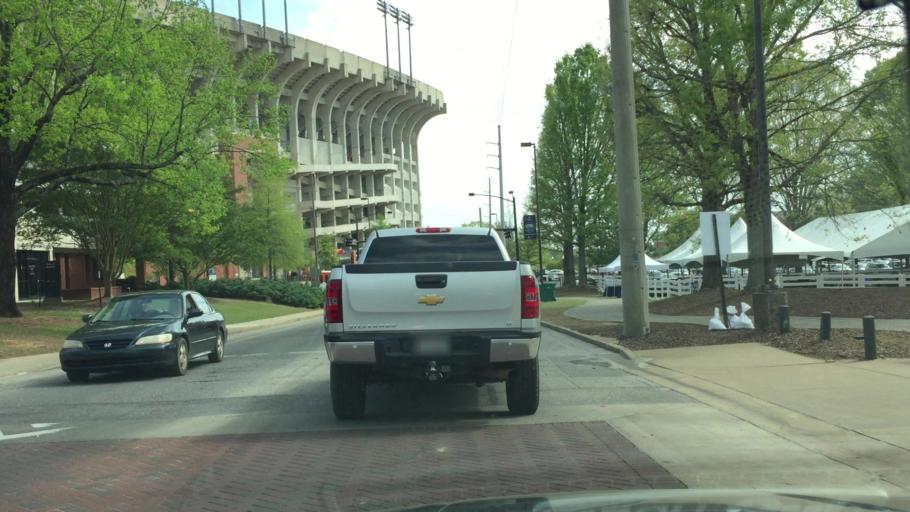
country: US
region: Alabama
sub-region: Lee County
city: Auburn
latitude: 32.6041
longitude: -85.4904
